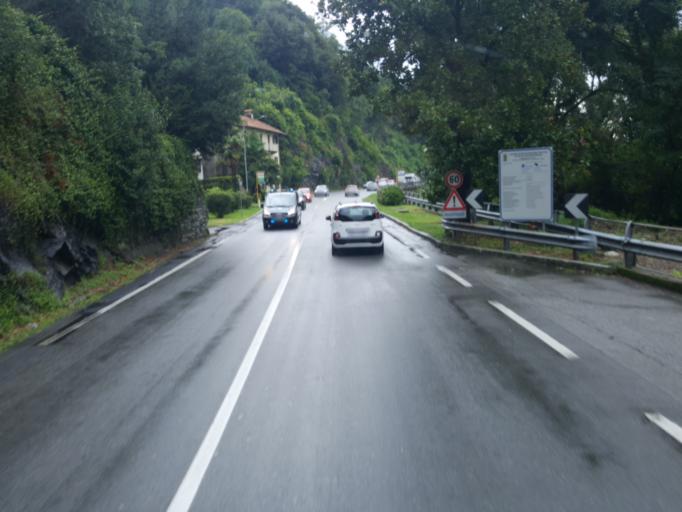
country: IT
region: Piedmont
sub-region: Provincia Verbano-Cusio-Ossola
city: Santino
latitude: 45.9405
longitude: 8.5096
